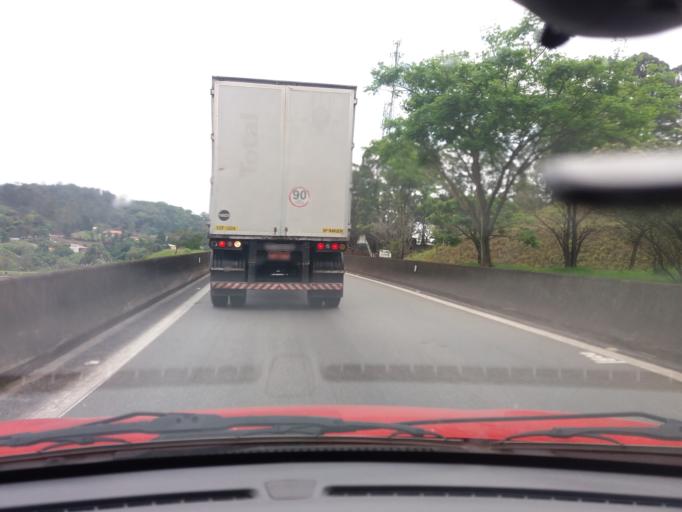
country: BR
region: Sao Paulo
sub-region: Caieiras
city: Caieiras
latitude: -23.4314
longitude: -46.7588
